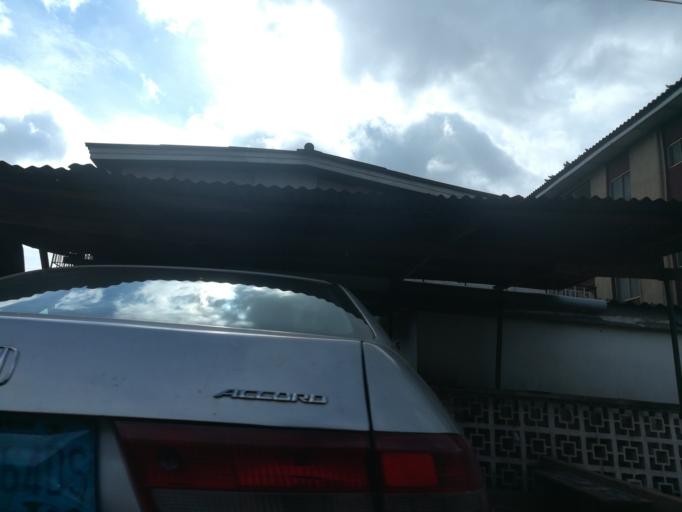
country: NG
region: Lagos
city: Somolu
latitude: 6.5444
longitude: 3.3760
